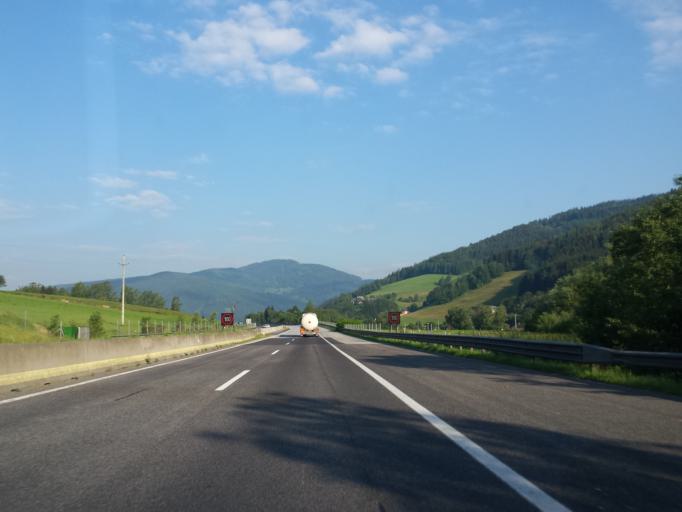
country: AT
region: Styria
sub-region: Politischer Bezirk Bruck-Muerzzuschlag
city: Muerzzuschlag
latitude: 47.6027
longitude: 15.7151
